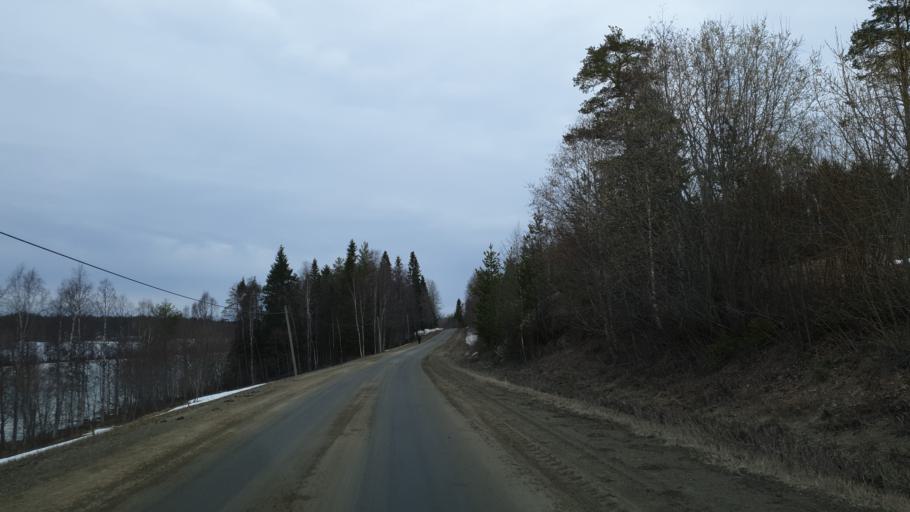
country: SE
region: Vaesterbotten
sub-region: Skelleftea Kommun
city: Burea
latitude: 64.3196
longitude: 21.1389
